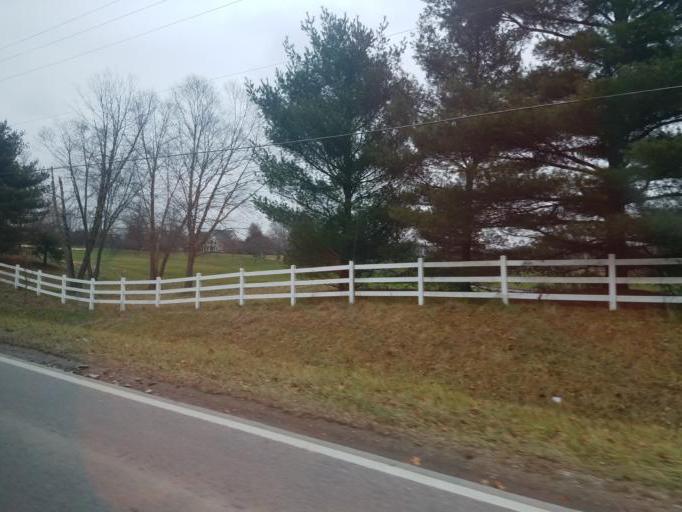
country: US
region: Ohio
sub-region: Franklin County
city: Westerville
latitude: 40.1687
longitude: -82.9533
